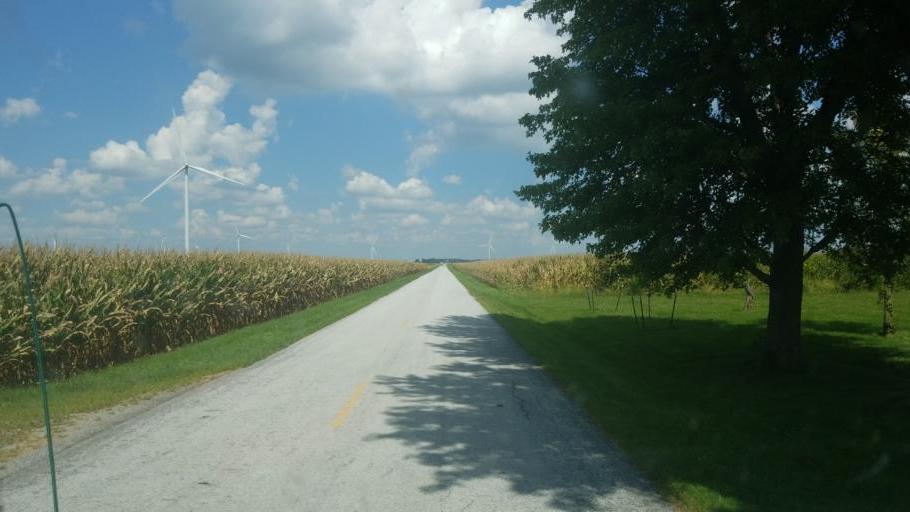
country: US
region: Ohio
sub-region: Hardin County
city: Ada
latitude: 40.7641
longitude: -83.7287
